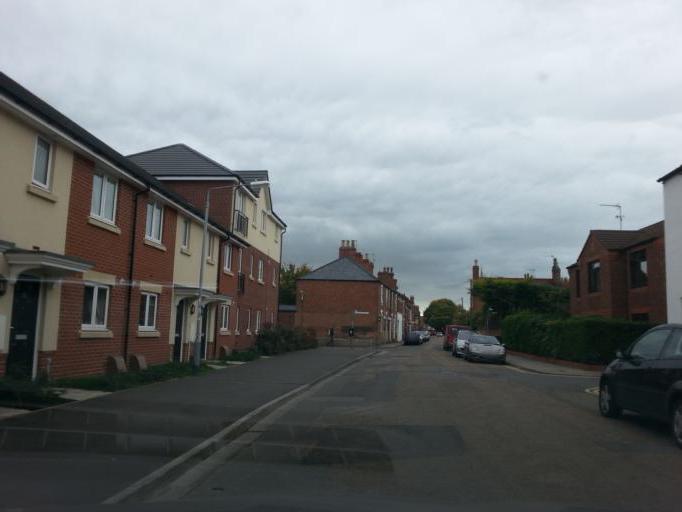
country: GB
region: England
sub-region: Nottinghamshire
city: Newark on Trent
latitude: 53.0739
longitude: -0.8007
